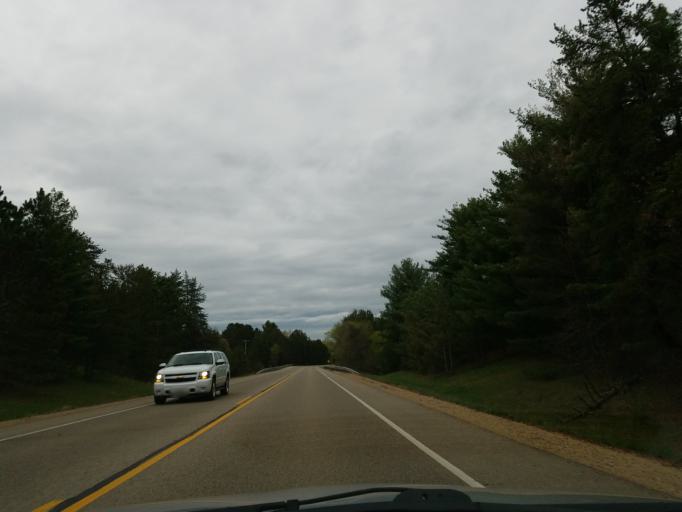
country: US
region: Wisconsin
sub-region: Saint Croix County
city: North Hudson
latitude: 45.0207
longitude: -92.7452
